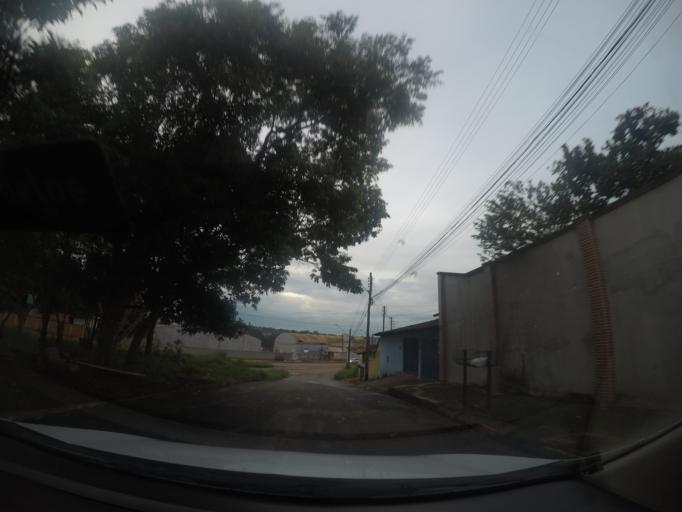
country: BR
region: Goias
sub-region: Goiania
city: Goiania
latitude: -16.6315
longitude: -49.2390
